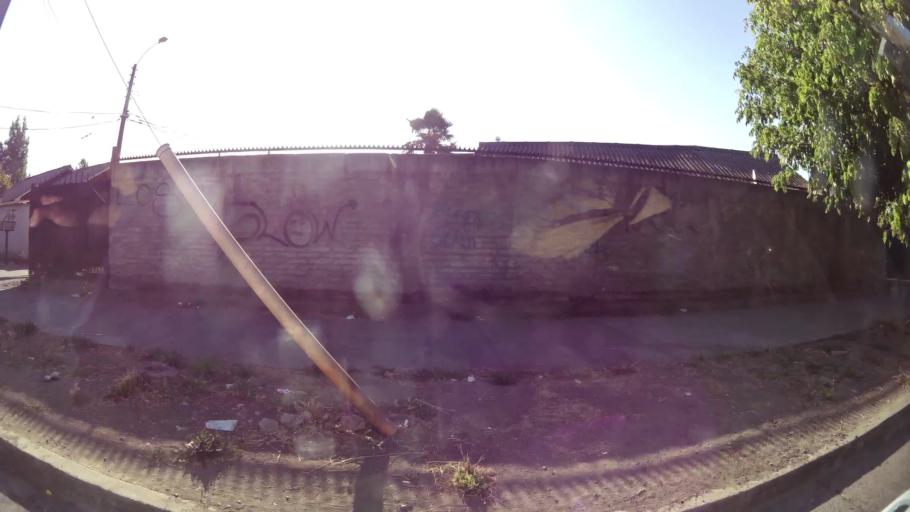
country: CL
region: Maule
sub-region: Provincia de Talca
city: Talca
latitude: -35.4368
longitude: -71.6734
